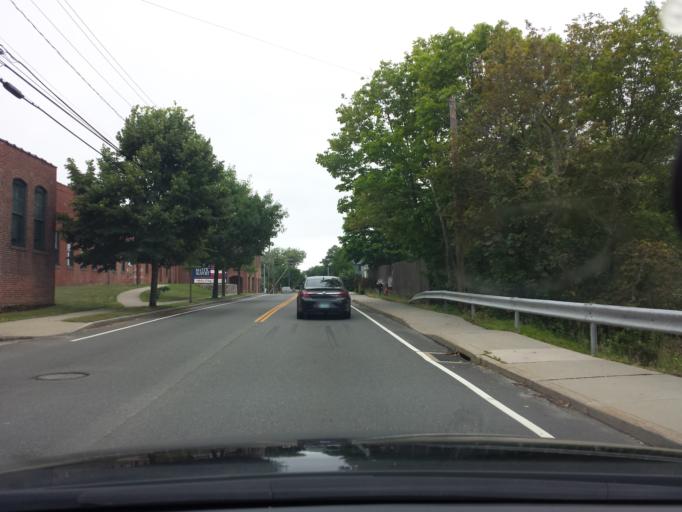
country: US
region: Connecticut
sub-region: New London County
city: Mystic
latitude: 41.3651
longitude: -71.9628
